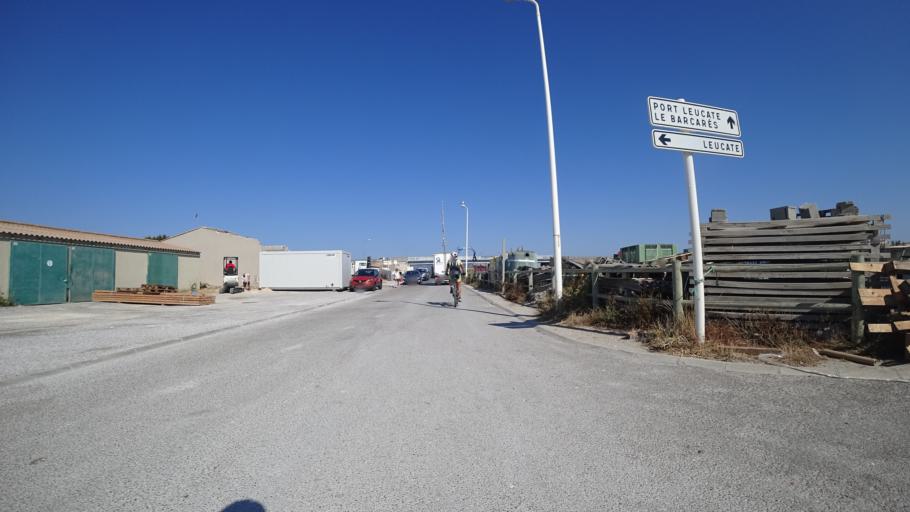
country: FR
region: Languedoc-Roussillon
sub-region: Departement de l'Aude
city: Leucate
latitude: 42.8854
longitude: 3.0492
